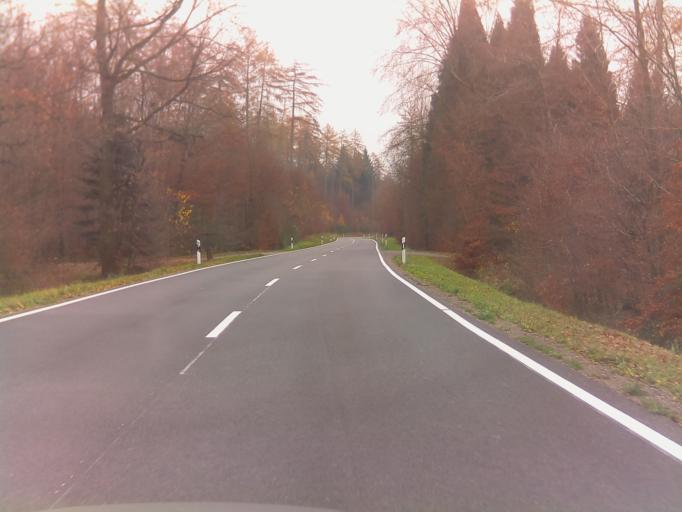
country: DE
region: Baden-Wuerttemberg
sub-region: Karlsruhe Region
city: Neunkirchen
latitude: 49.3993
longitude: 8.9896
